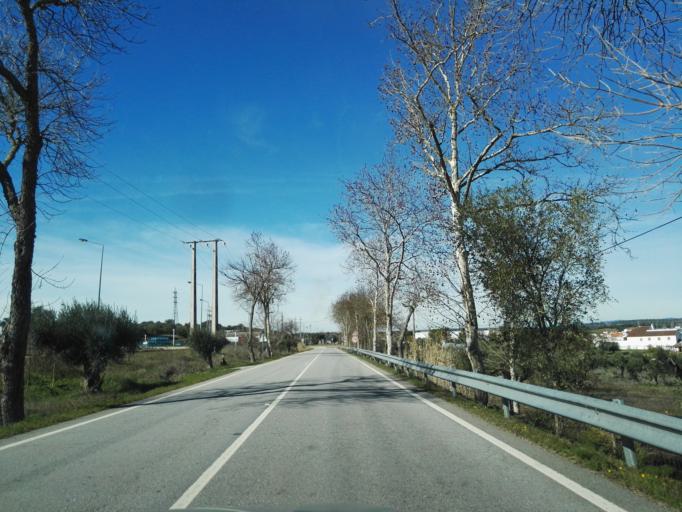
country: PT
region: Portalegre
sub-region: Arronches
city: Arronches
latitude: 39.1138
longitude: -7.2853
